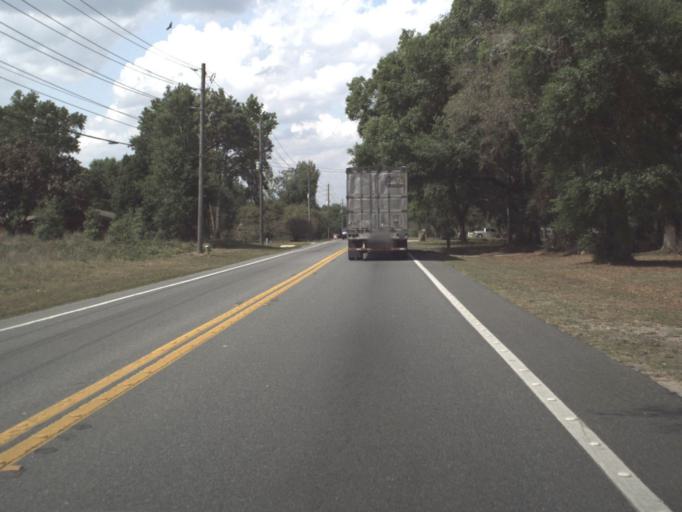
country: US
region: Florida
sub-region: Lake County
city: Groveland
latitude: 28.5717
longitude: -81.8556
